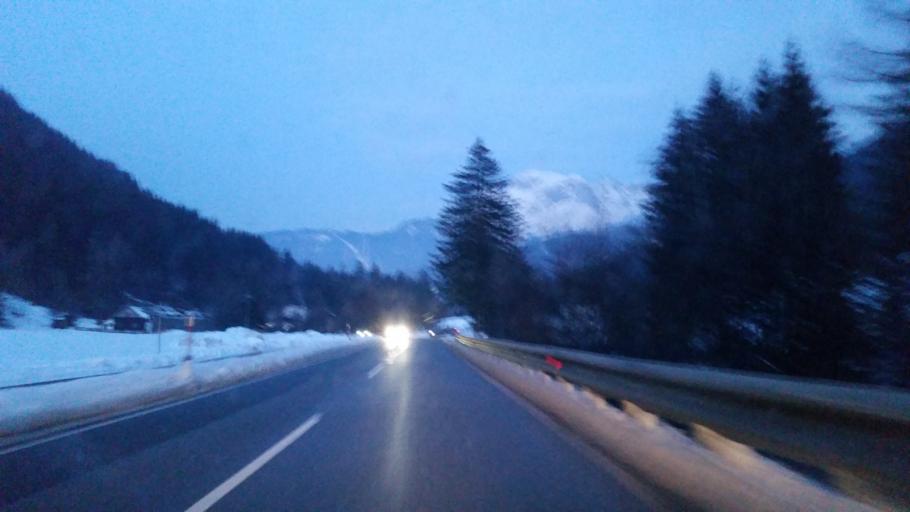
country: AT
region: Salzburg
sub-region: Politischer Bezirk Hallein
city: Abtenau
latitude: 47.4979
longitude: 13.4119
